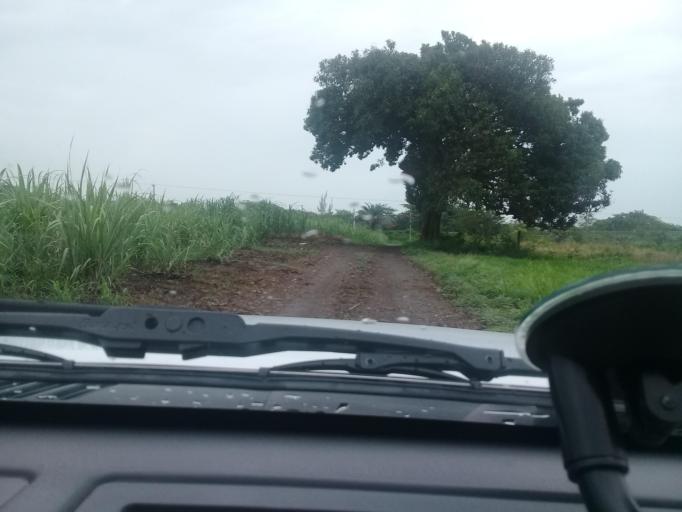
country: MX
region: Veracruz
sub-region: Puente Nacional
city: Cabezas
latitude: 19.3662
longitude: -96.3890
